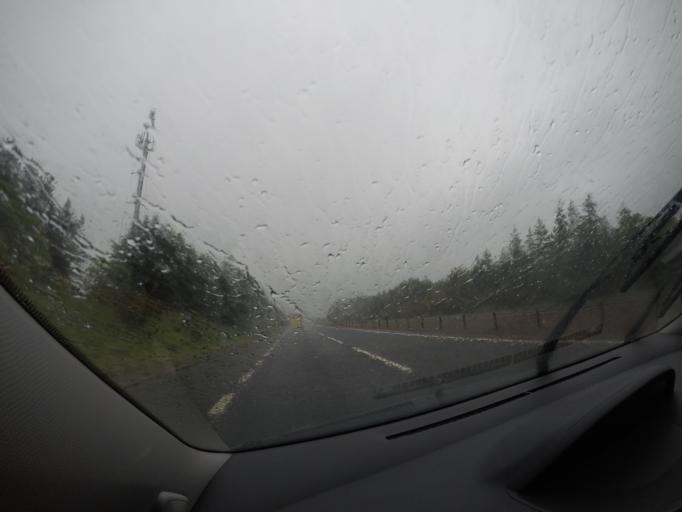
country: GB
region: Scotland
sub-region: Dundee City
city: Dundee
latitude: 56.5497
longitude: -2.9381
